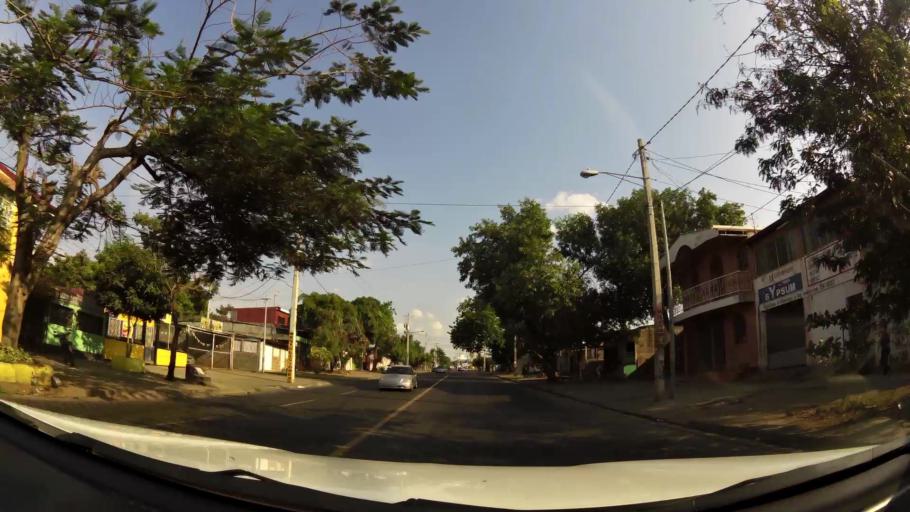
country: NI
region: Managua
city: Managua
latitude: 12.1352
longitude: -86.2584
